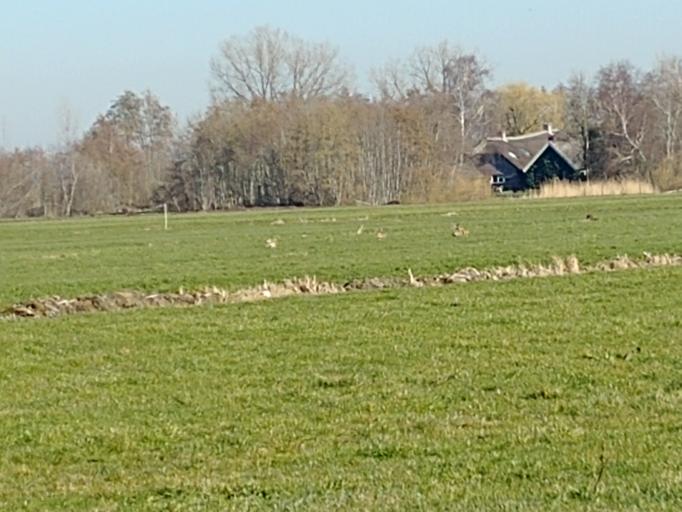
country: NL
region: Utrecht
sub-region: Gemeente Woerden
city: Woerden
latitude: 52.1259
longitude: 4.8754
